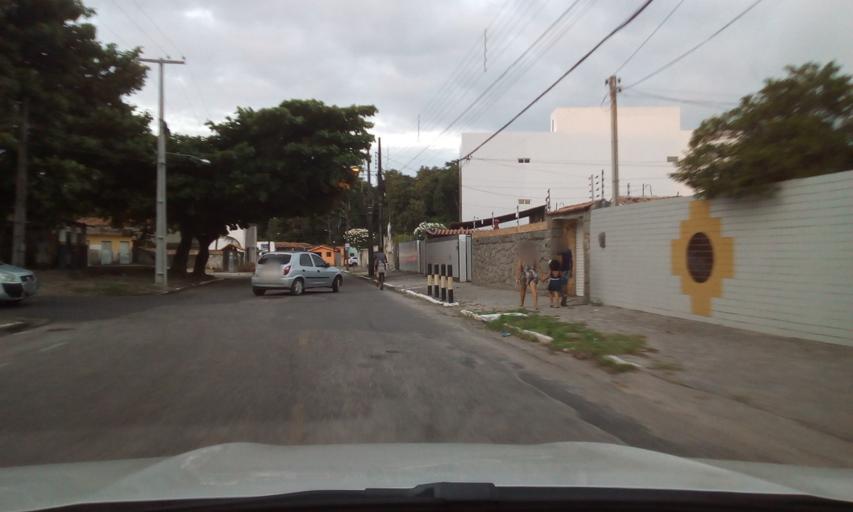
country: BR
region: Paraiba
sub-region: Joao Pessoa
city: Joao Pessoa
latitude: -7.1604
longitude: -34.8669
